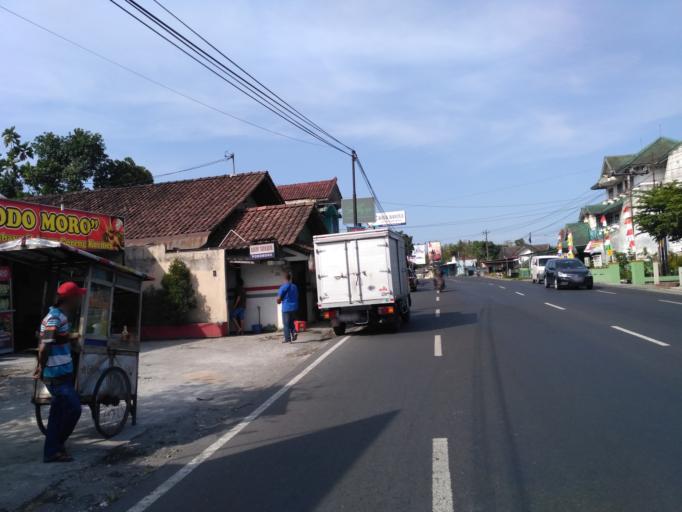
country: ID
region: Daerah Istimewa Yogyakarta
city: Godean
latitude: -7.8121
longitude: 110.2721
